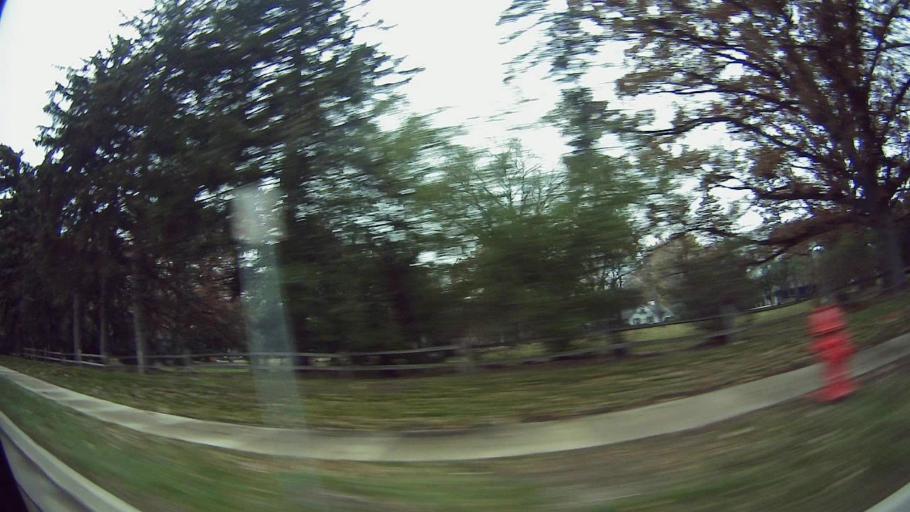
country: US
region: Michigan
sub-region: Oakland County
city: Franklin
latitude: 42.5484
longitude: -83.2854
